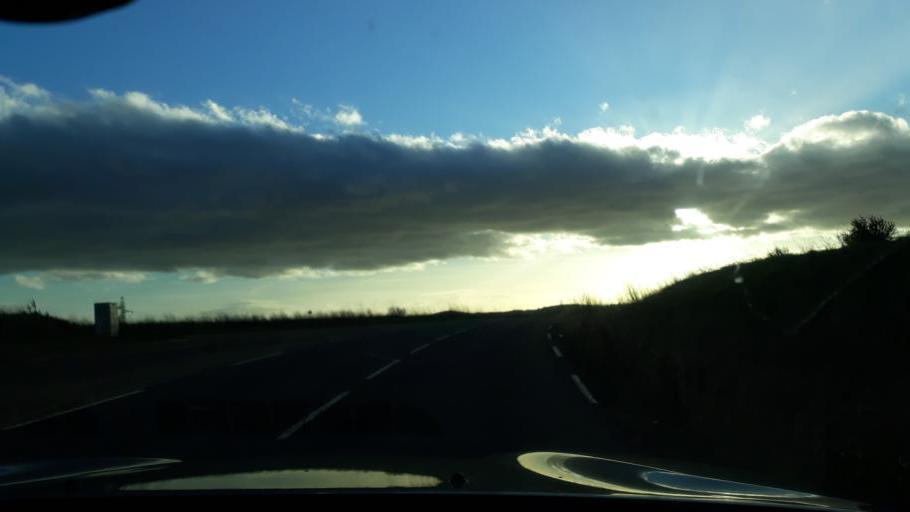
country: FR
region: Languedoc-Roussillon
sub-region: Departement de l'Herault
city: Colombiers
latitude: 43.3057
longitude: 3.1371
